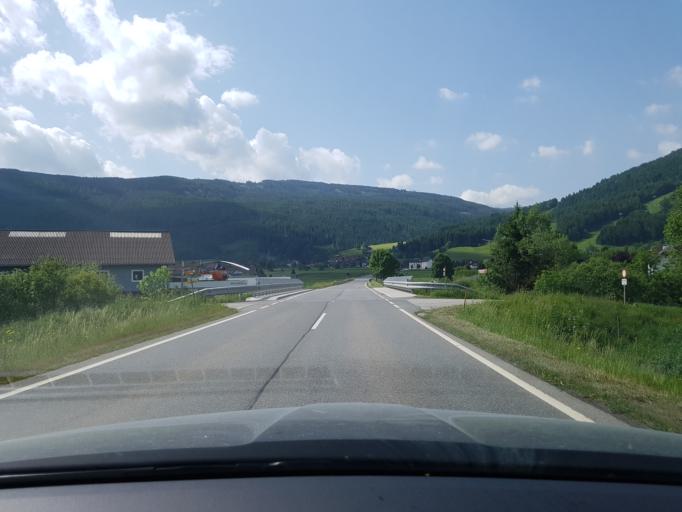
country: AT
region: Salzburg
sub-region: Politischer Bezirk Tamsweg
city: Sankt Margarethen im Lungau
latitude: 47.0881
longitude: 13.6926
